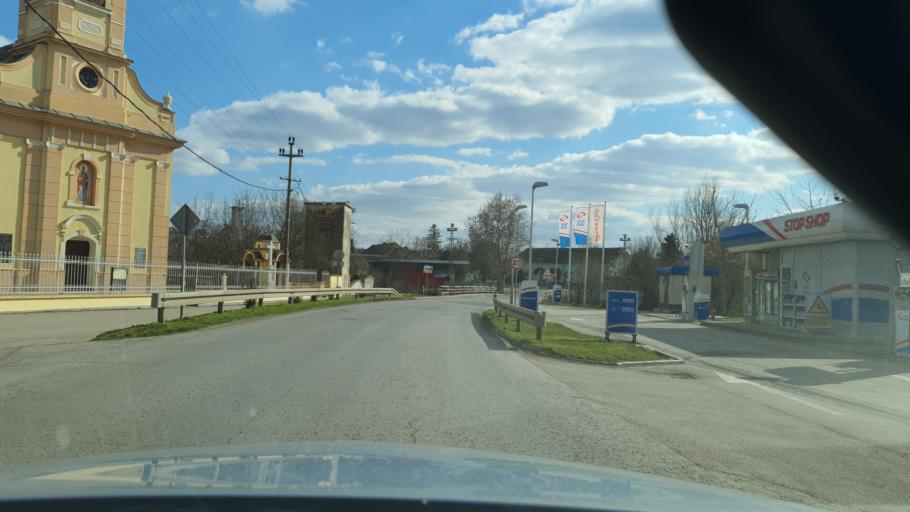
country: RS
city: Zmajevo
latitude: 45.4543
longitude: 19.6874
